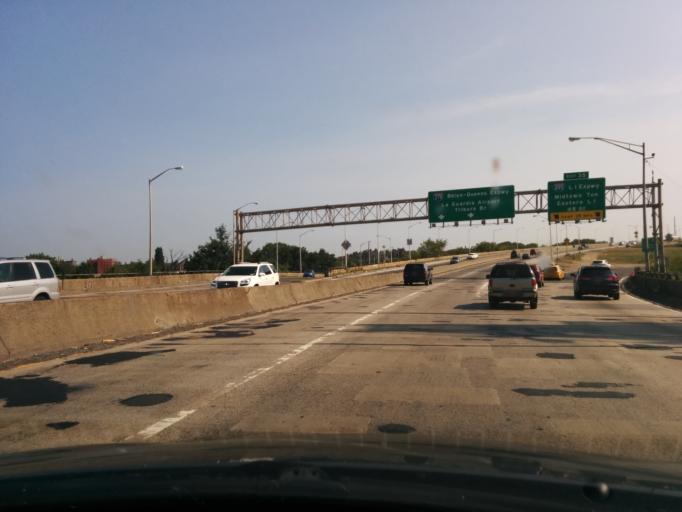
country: US
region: New York
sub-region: Queens County
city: Long Island City
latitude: 40.7320
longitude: -73.9255
